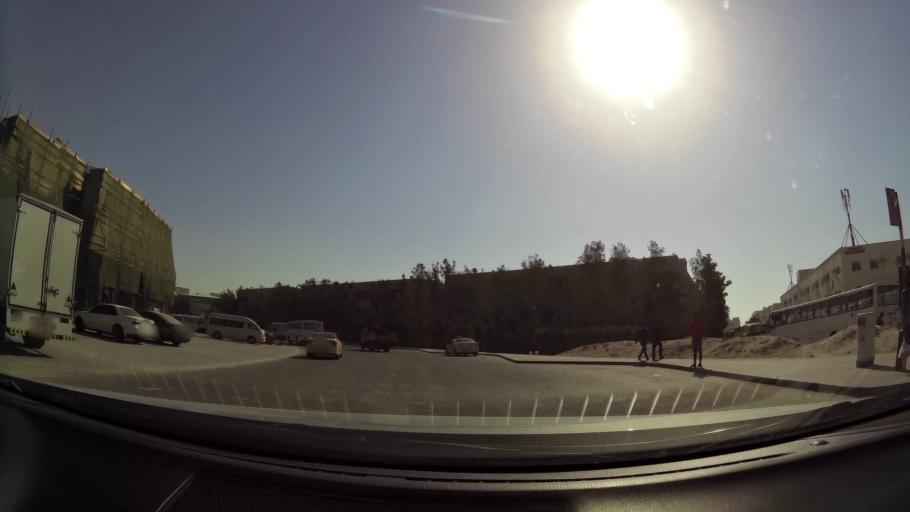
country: AE
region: Dubai
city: Dubai
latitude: 25.0073
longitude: 55.1059
